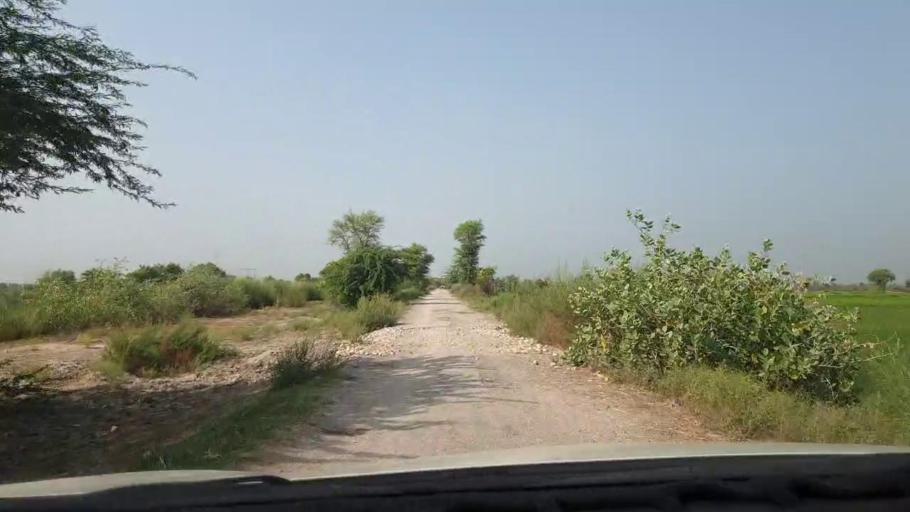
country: PK
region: Sindh
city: Goth Garelo
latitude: 27.4585
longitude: 68.1261
